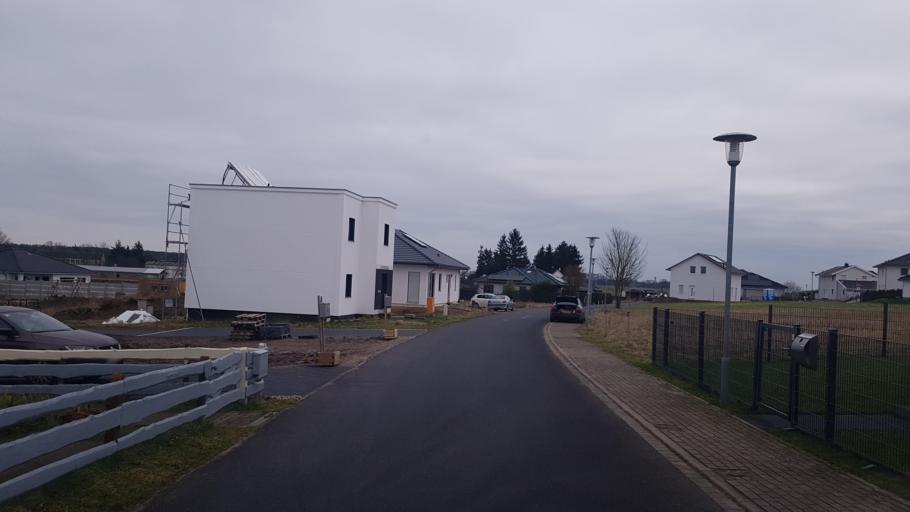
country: DE
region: Brandenburg
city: Oranienburg
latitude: 52.8711
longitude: 13.2240
